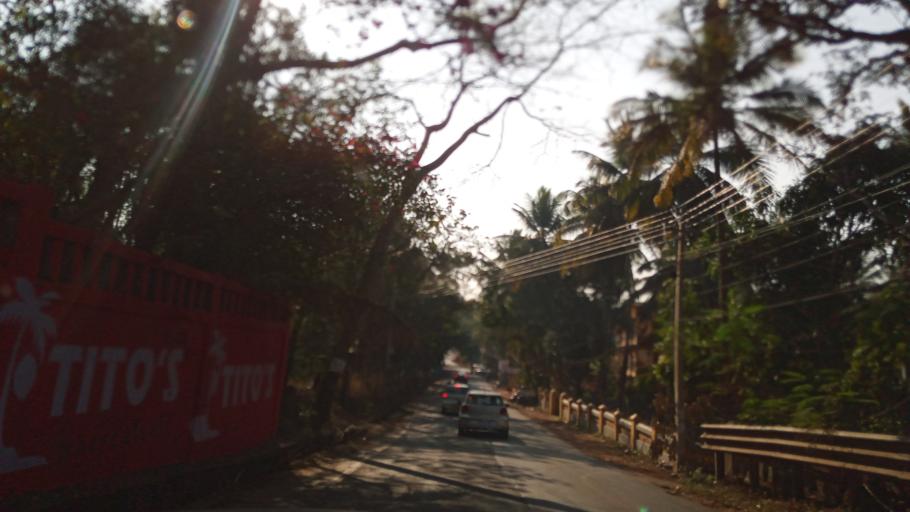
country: IN
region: Goa
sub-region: North Goa
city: Saligao
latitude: 15.5435
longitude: 73.8139
